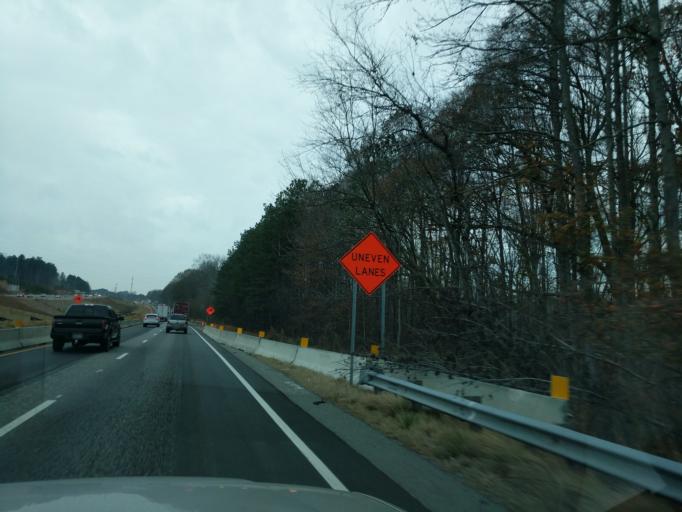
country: US
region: Georgia
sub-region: Gwinnett County
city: Sugar Hill
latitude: 34.0530
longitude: -84.0145
